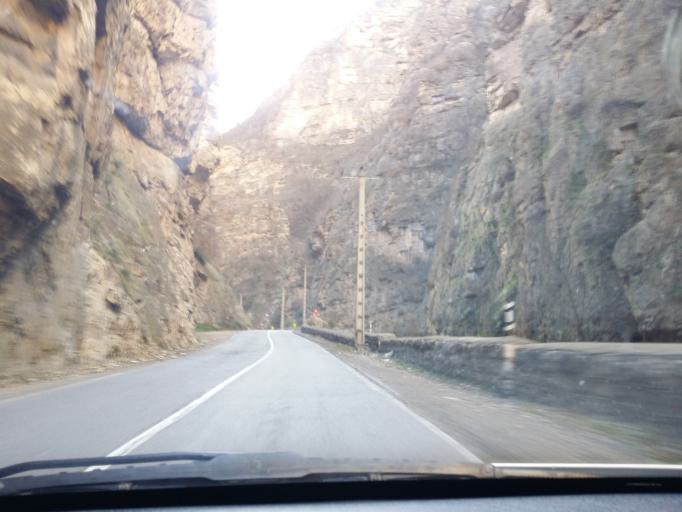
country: IR
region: Mazandaran
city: Chalus
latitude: 36.2724
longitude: 51.2447
